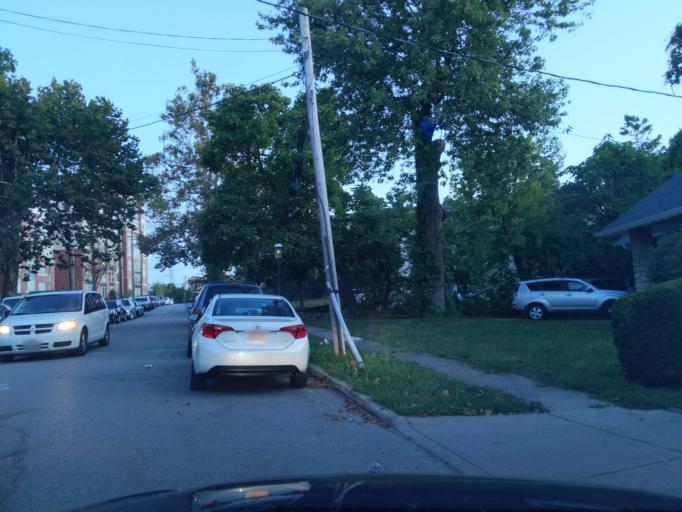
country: US
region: Ohio
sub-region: Hamilton County
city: Saint Bernard
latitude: 39.1312
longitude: -84.5241
